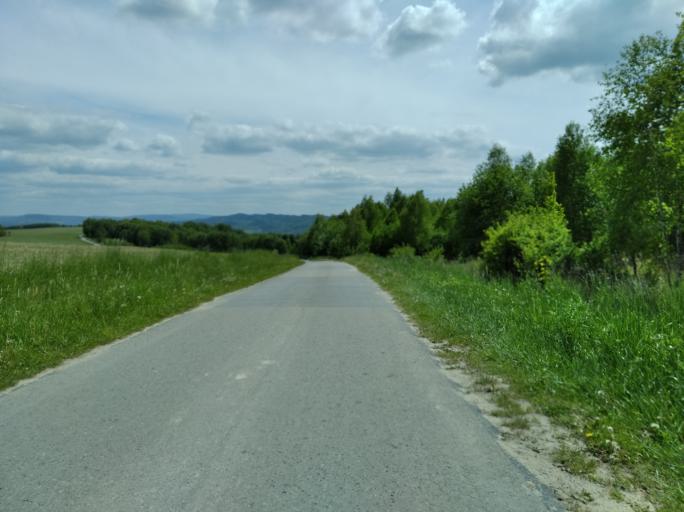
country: PL
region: Subcarpathian Voivodeship
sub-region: Powiat ropczycko-sedziszowski
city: Wielopole Skrzynskie
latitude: 49.8979
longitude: 21.6112
